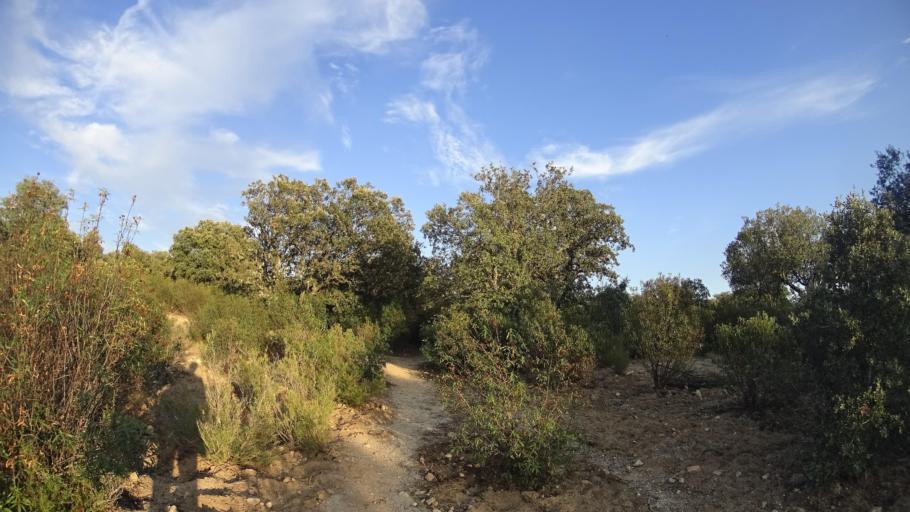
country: ES
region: Madrid
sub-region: Provincia de Madrid
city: Colmenarejo
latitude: 40.5609
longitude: -4.0441
